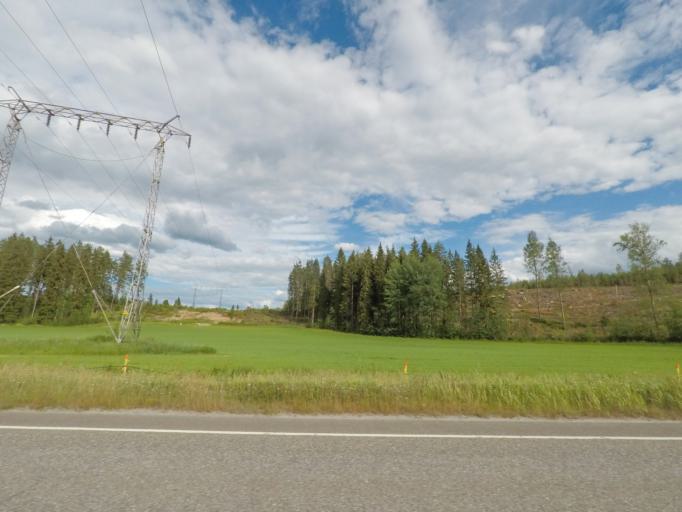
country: FI
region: Uusimaa
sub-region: Porvoo
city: Pukkila
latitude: 60.8004
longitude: 25.4733
